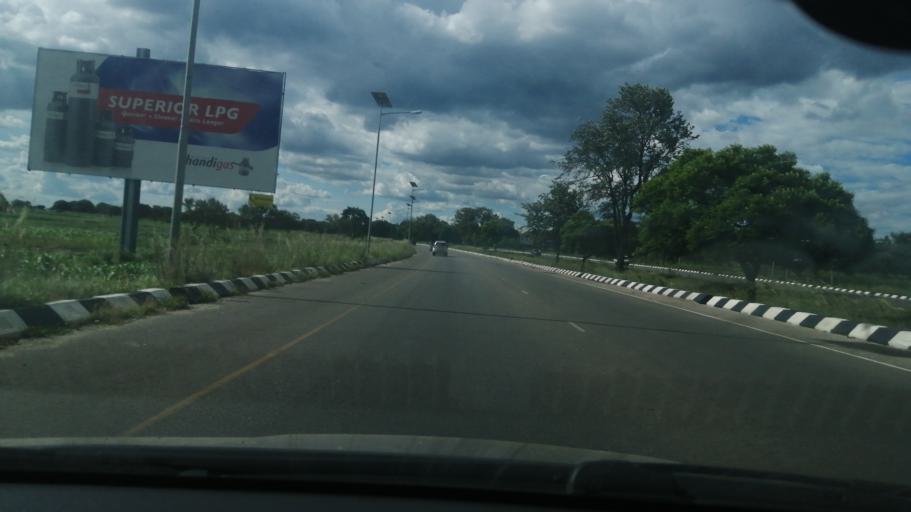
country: ZW
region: Harare
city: Harare
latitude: -17.8640
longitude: 31.0705
